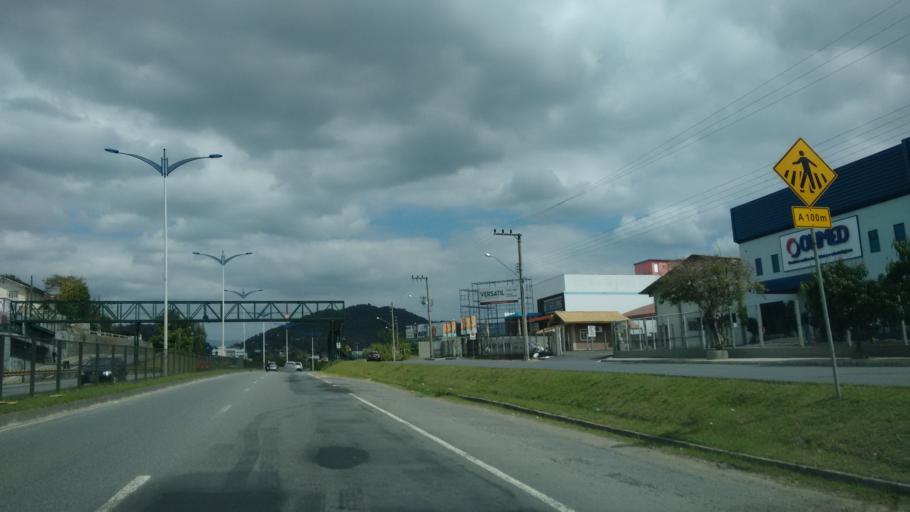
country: BR
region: Santa Catarina
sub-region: Blumenau
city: Blumenau
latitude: -26.8867
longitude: -49.0697
